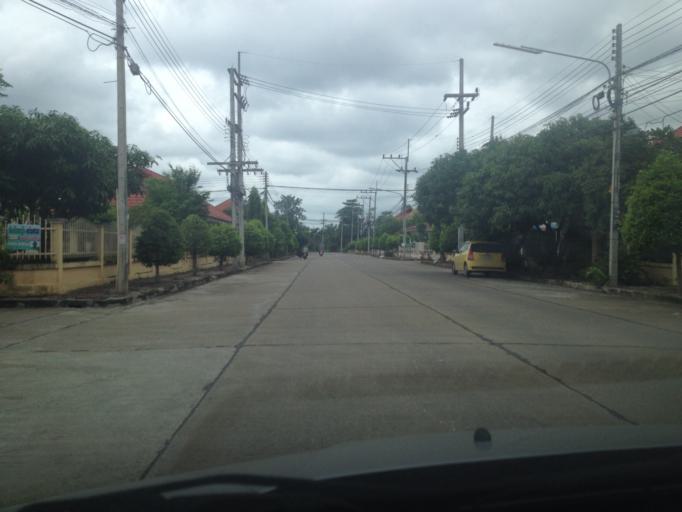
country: TH
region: Chiang Mai
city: Hang Dong
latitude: 18.6988
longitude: 98.9205
